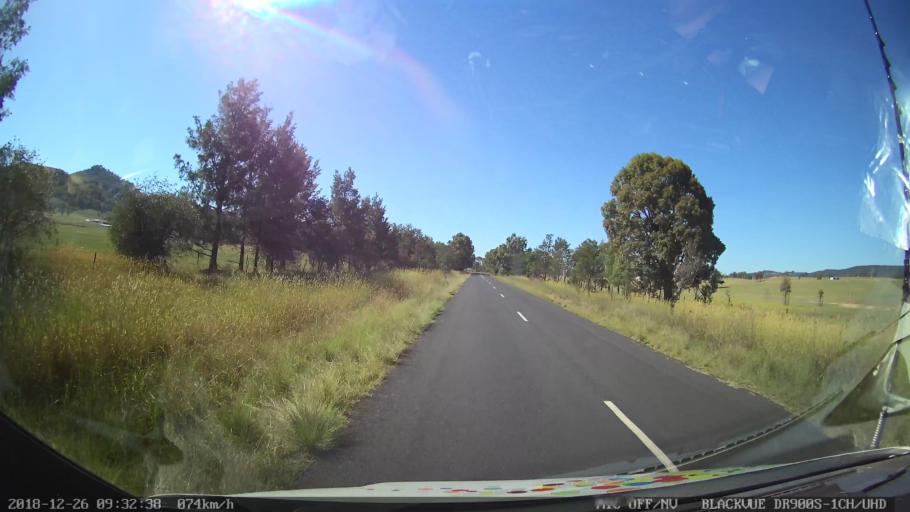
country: AU
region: New South Wales
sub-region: Mid-Western Regional
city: Kandos
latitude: -32.8866
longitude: 150.0327
